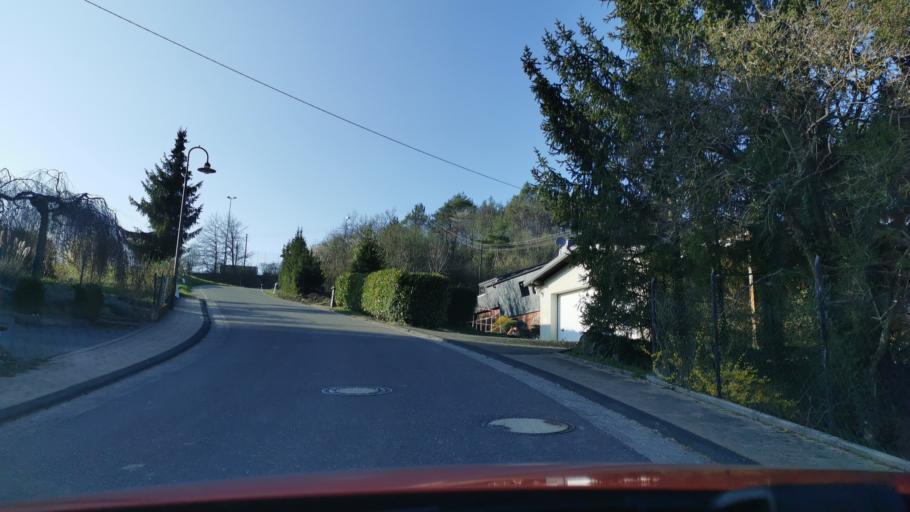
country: DE
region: Rheinland-Pfalz
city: Trierweiler
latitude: 49.7783
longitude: 6.5474
